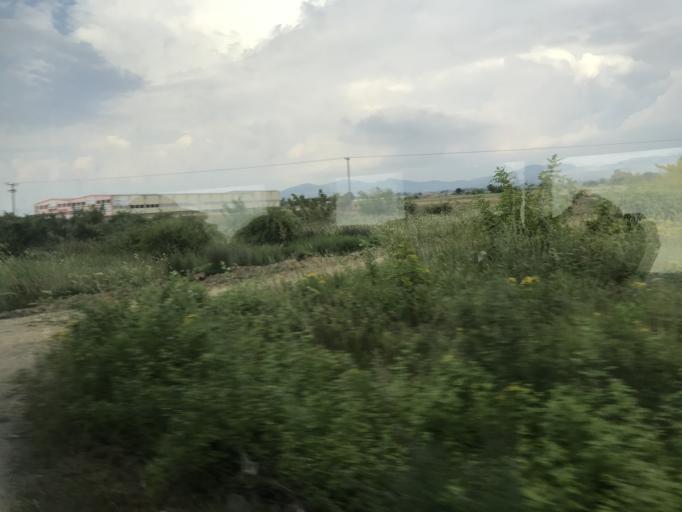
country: GR
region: East Macedonia and Thrace
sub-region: Nomos Rodopis
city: Sapes
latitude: 40.9730
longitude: 25.6437
